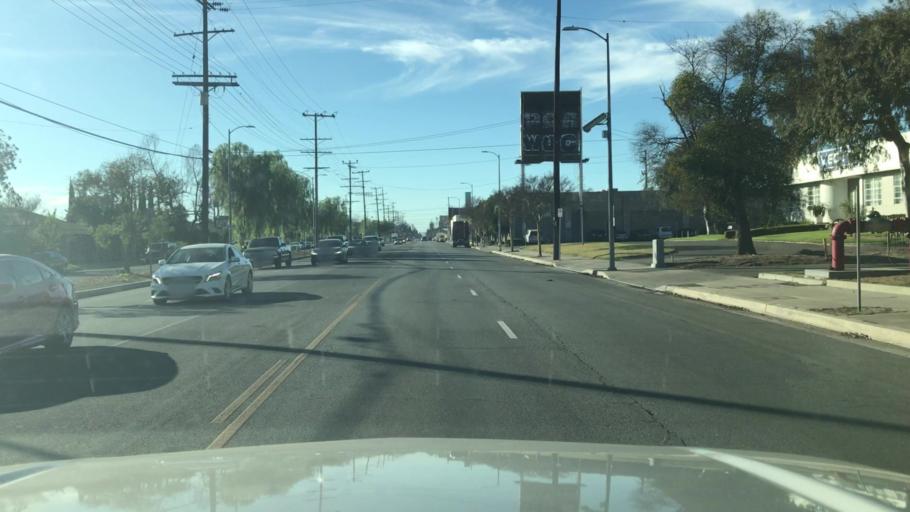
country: US
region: California
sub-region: Los Angeles County
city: North Hollywood
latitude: 34.1940
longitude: -118.3721
